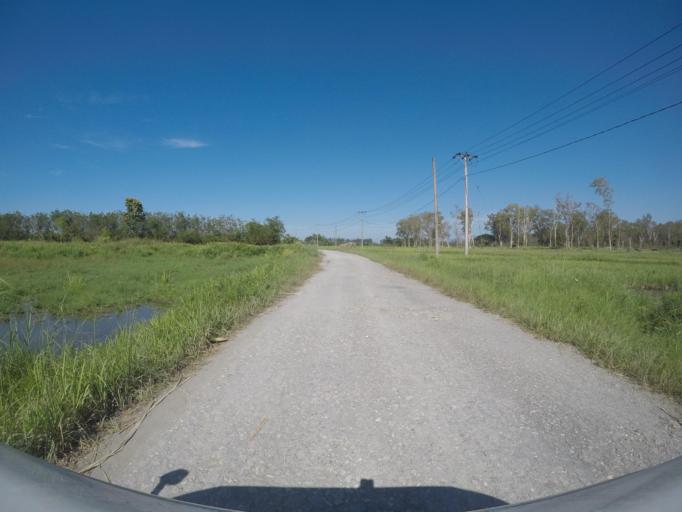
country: TL
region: Viqueque
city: Viqueque
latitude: -8.9361
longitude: 126.1196
